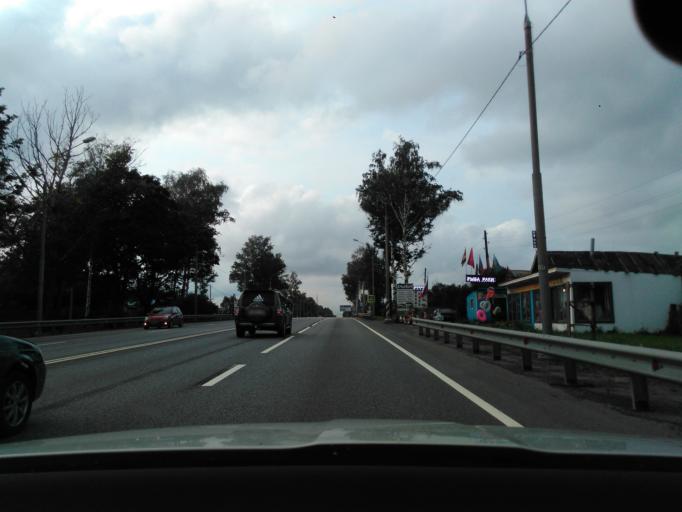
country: RU
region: Tverskaya
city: Zavidovo
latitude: 56.5509
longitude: 36.5145
